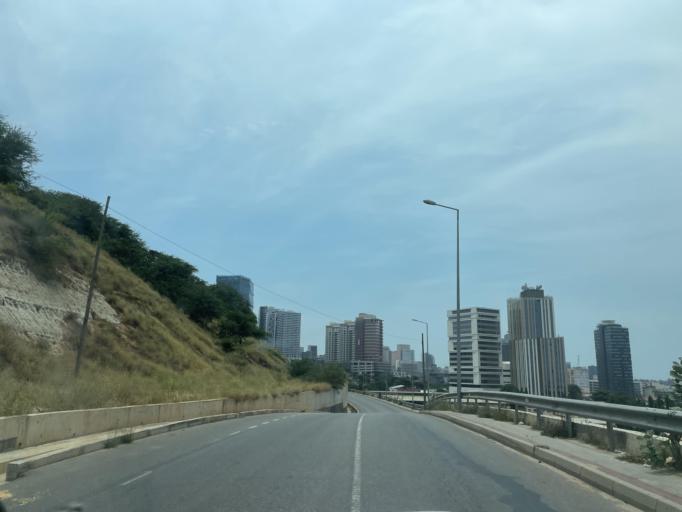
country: AO
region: Luanda
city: Luanda
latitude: -8.8071
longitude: 13.2465
